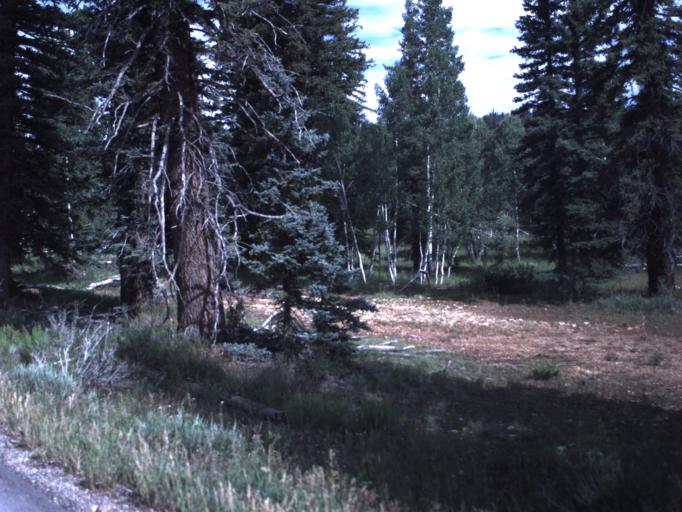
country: US
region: Utah
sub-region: Iron County
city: Parowan
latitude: 37.5141
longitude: -112.6902
